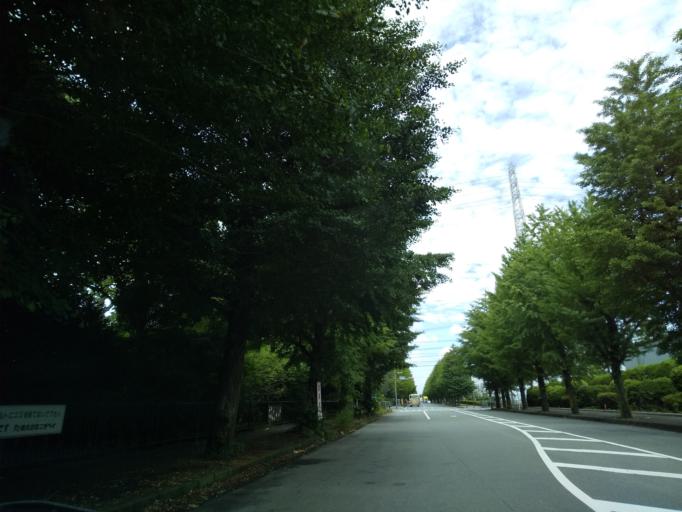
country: JP
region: Kanagawa
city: Zama
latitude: 35.5169
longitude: 139.3478
